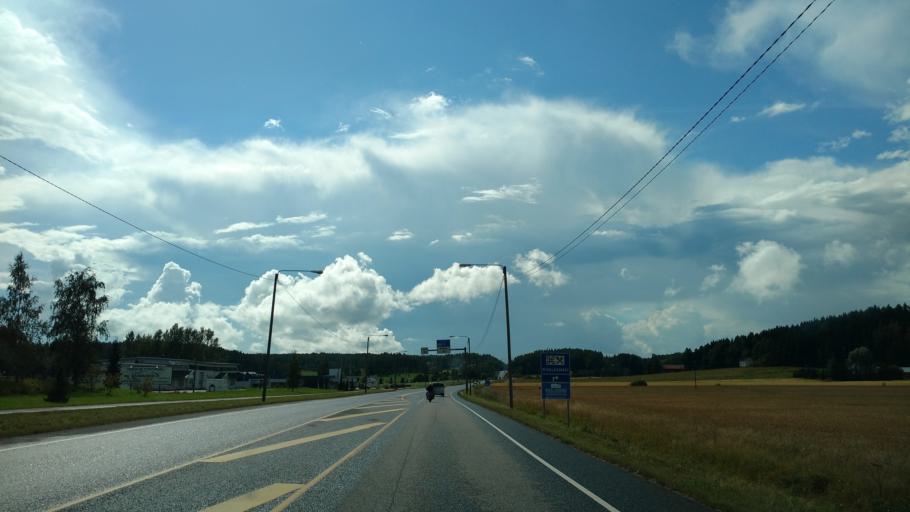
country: FI
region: Varsinais-Suomi
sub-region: Salo
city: Halikko
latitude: 60.3879
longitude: 23.0657
